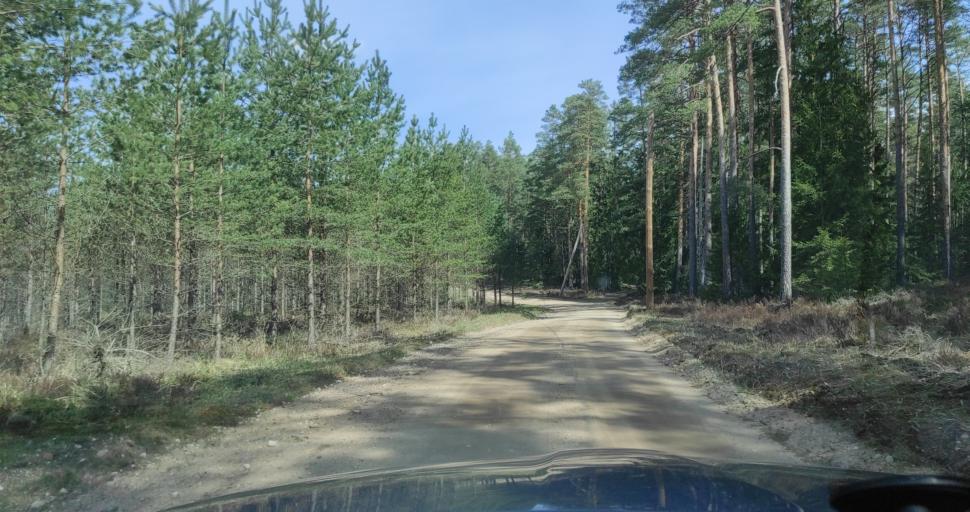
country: LV
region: Talsu Rajons
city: Stende
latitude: 57.1447
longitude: 22.2798
